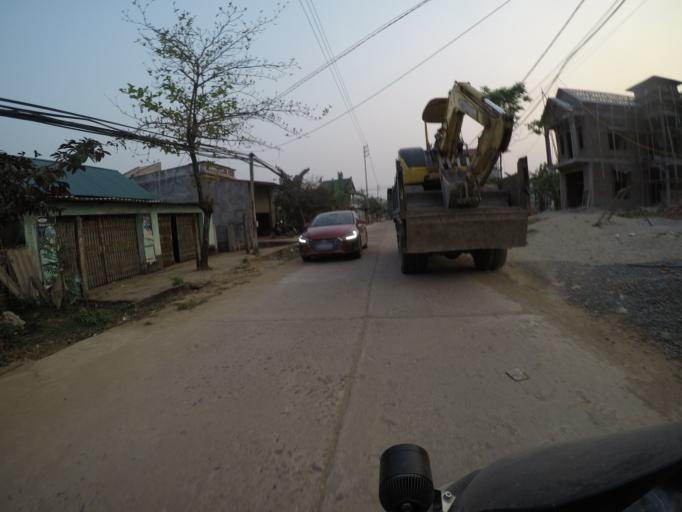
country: VN
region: Vinh Phuc
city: Trai Ngau
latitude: 21.4622
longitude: 105.5700
